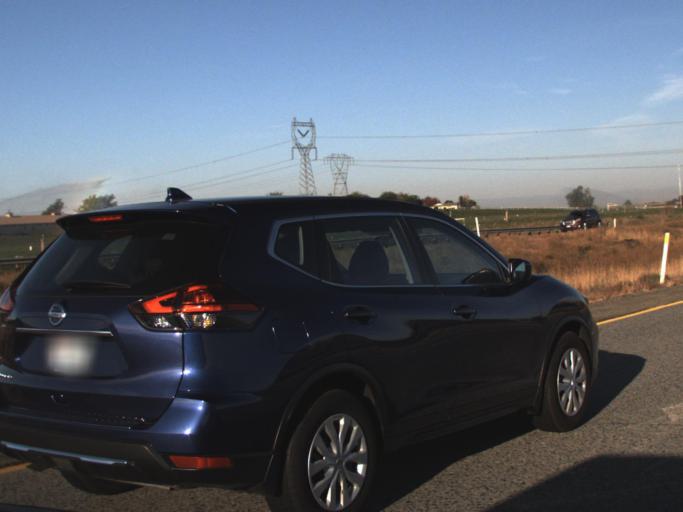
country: US
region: Washington
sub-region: Yakima County
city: Granger
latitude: 46.3365
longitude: -120.1301
